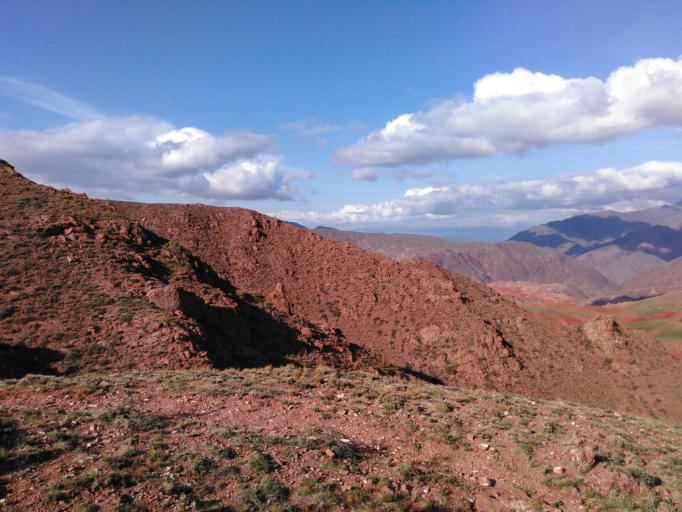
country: KG
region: Chuy
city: Bystrovka
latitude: 42.5829
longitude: 75.7449
